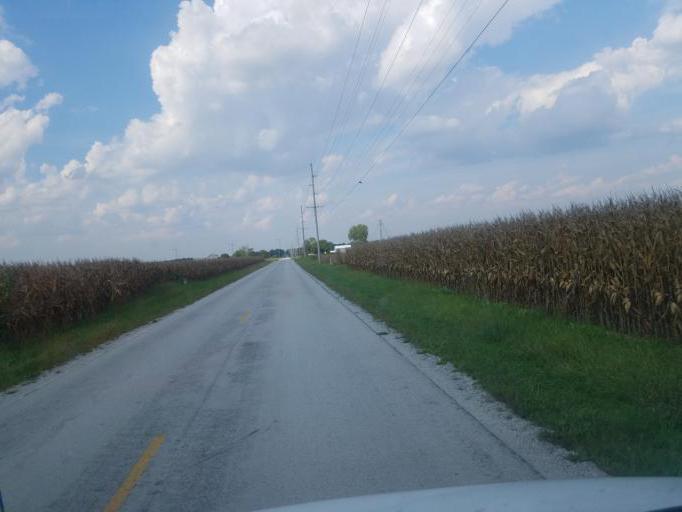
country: US
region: Ohio
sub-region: Hancock County
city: Arlington
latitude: 40.7678
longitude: -83.6522
